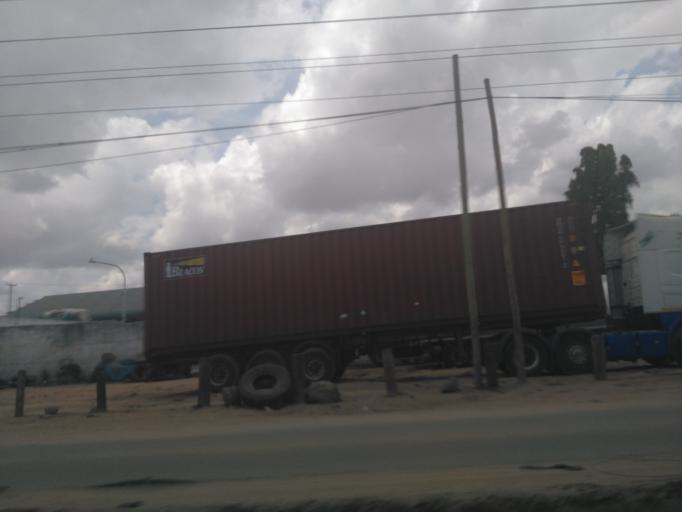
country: TZ
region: Dar es Salaam
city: Dar es Salaam
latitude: -6.8562
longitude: 39.2698
